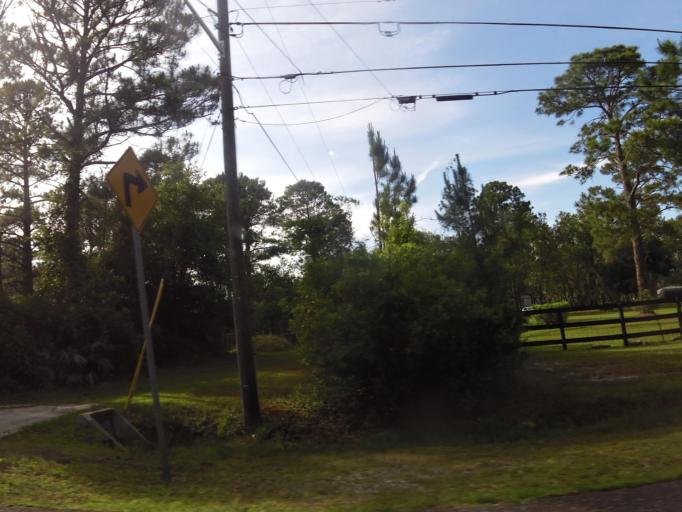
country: US
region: Florida
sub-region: Nassau County
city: Fernandina Beach
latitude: 30.5101
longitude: -81.4781
